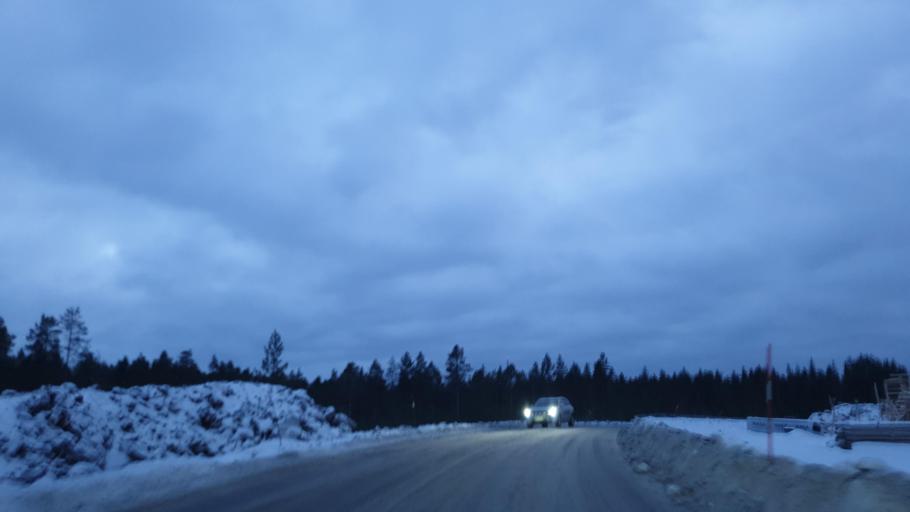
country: SE
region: Vaesterbotten
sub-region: Robertsfors Kommun
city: Robertsfors
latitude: 64.0162
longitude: 20.8295
